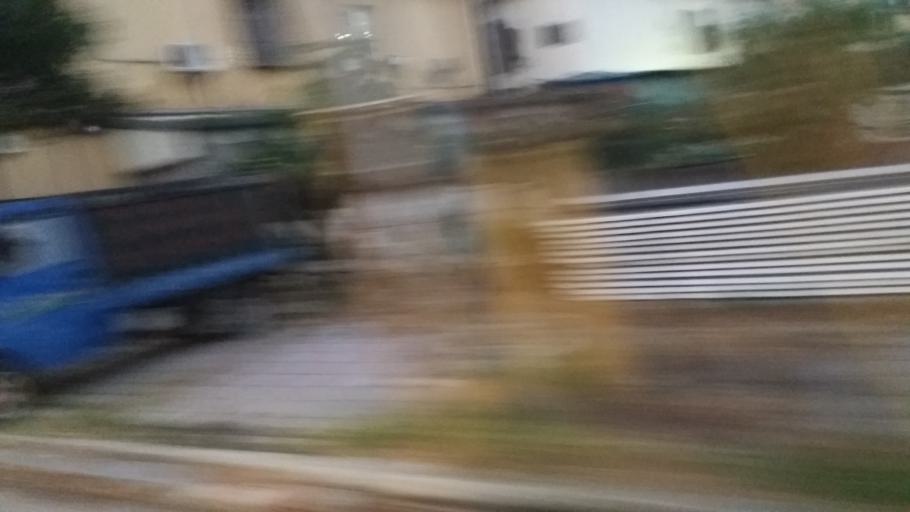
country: TW
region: Taiwan
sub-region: Hsinchu
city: Hsinchu
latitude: 24.7383
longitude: 120.9112
